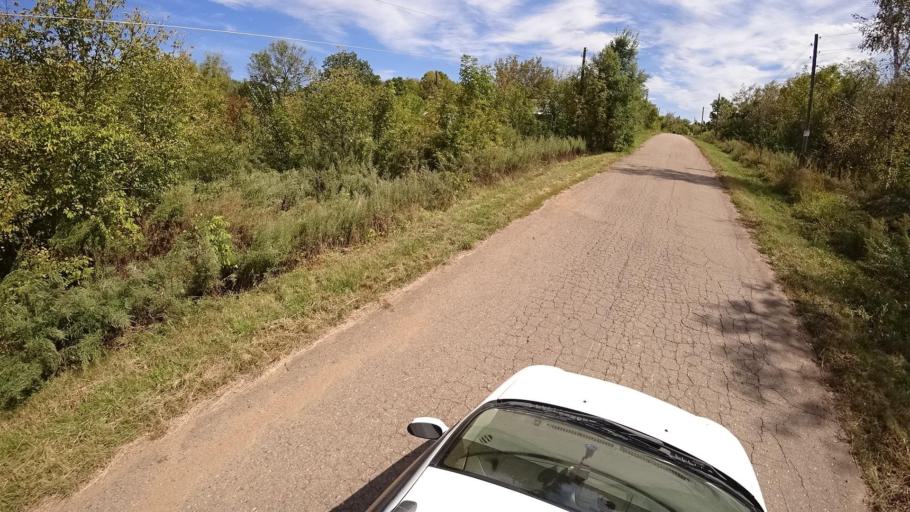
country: RU
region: Primorskiy
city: Yakovlevka
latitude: 44.6578
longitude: 133.7375
